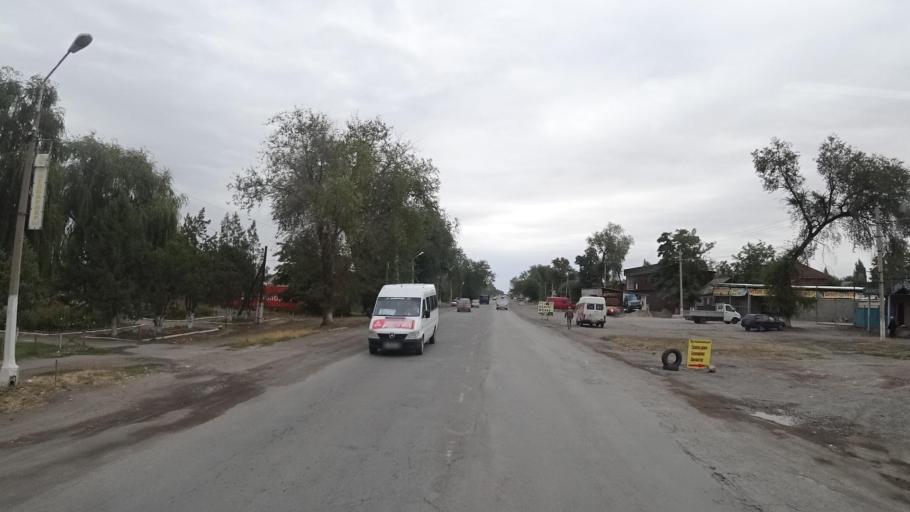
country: KG
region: Chuy
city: Kara-Balta
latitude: 42.8256
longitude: 73.8509
